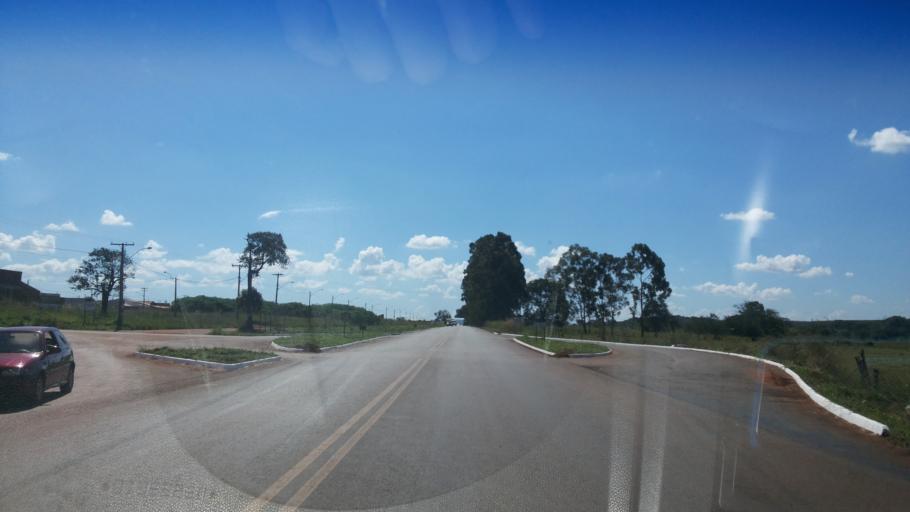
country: BR
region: Goias
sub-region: Goiania
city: Goiania
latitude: -16.5486
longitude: -49.2668
